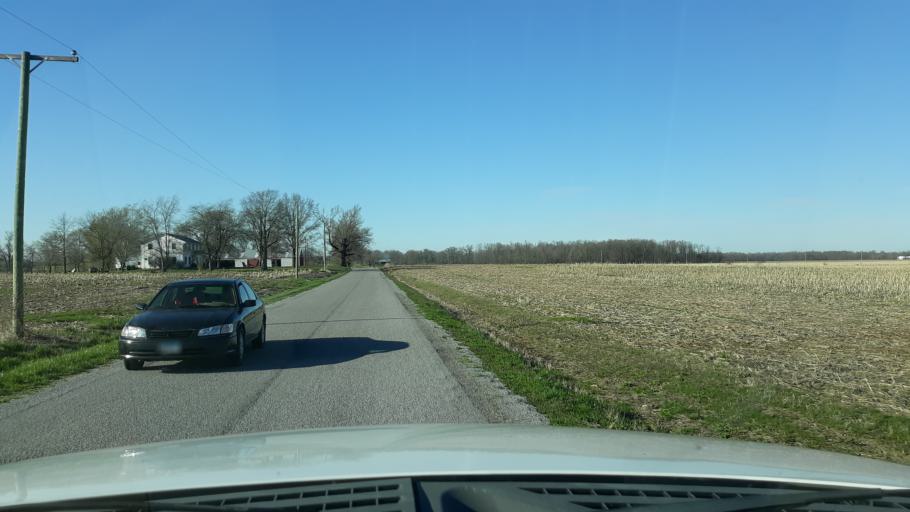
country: US
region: Illinois
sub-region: Saline County
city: Harrisburg
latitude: 37.7684
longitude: -88.5864
